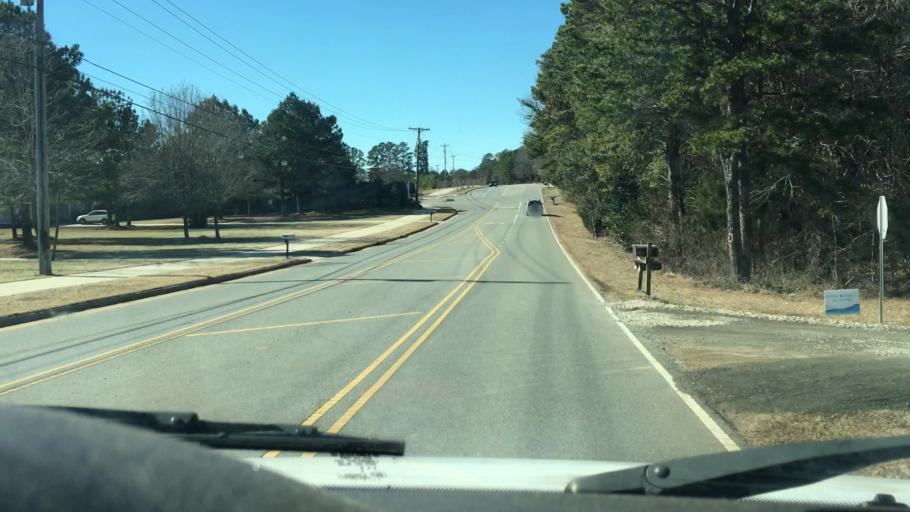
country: US
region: North Carolina
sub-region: Mecklenburg County
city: Cornelius
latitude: 35.4694
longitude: -80.8325
